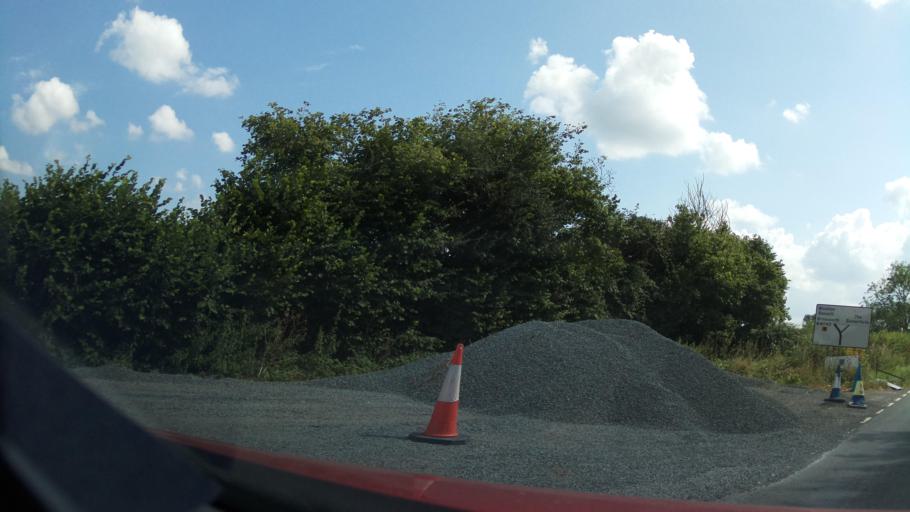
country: GB
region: England
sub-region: Wiltshire
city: Charlton
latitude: 51.5645
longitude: -2.0541
